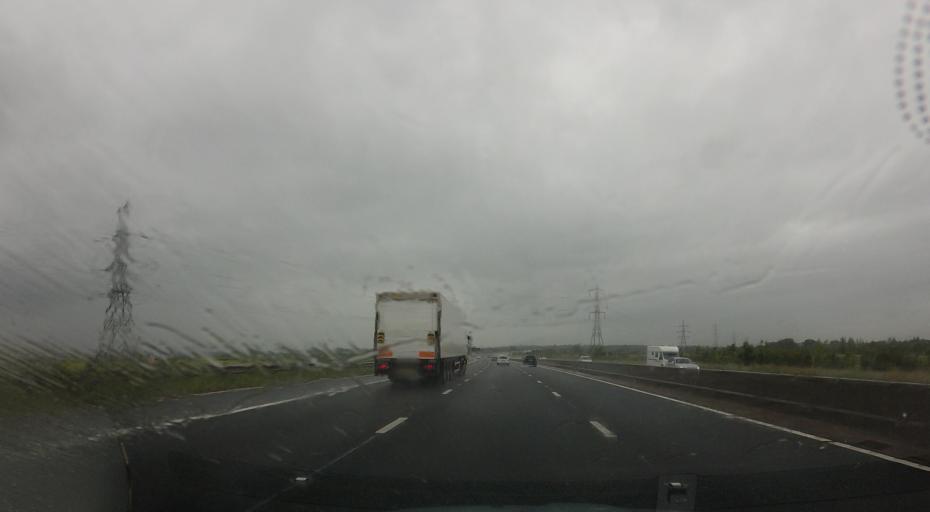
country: GB
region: Scotland
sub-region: Dumfries and Galloway
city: Gretna
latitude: 54.9830
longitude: -3.0299
